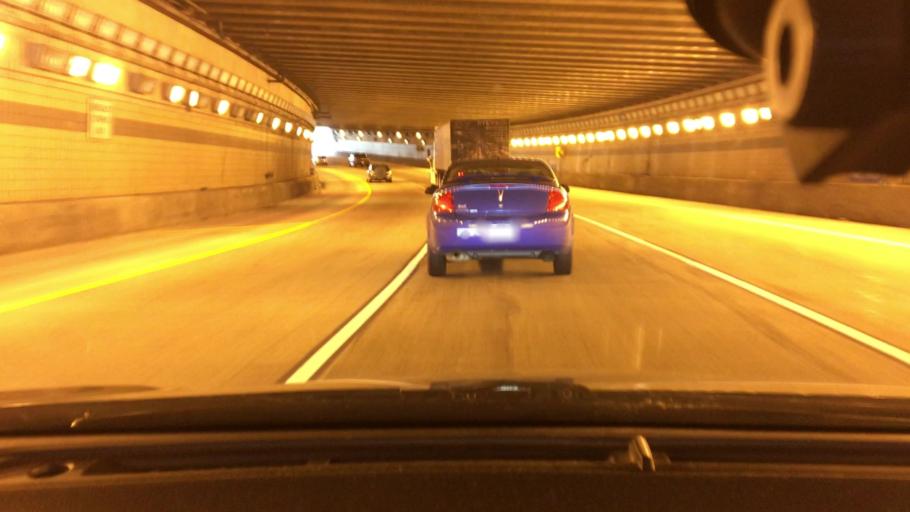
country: US
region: Wisconsin
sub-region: Milwaukee County
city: Saint Francis
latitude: 42.9607
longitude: -87.9340
